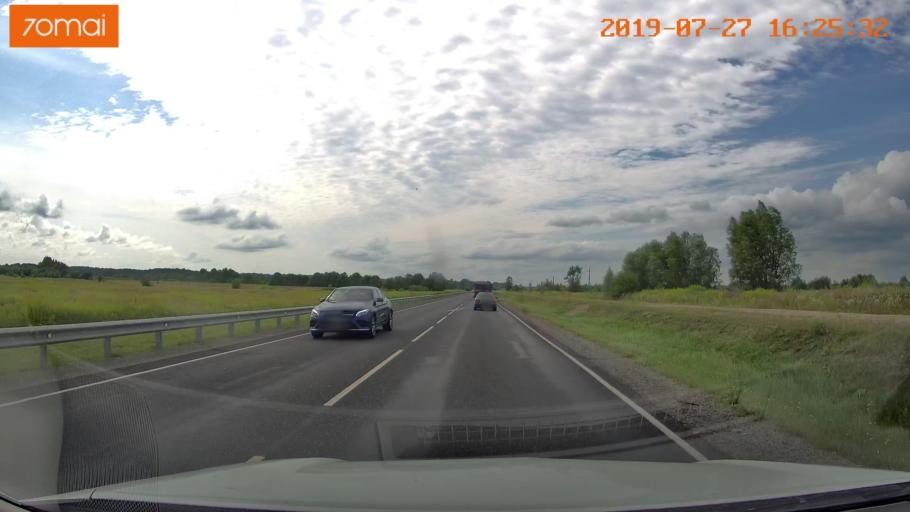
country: RU
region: Kaliningrad
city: Zheleznodorozhnyy
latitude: 54.6376
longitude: 21.4291
